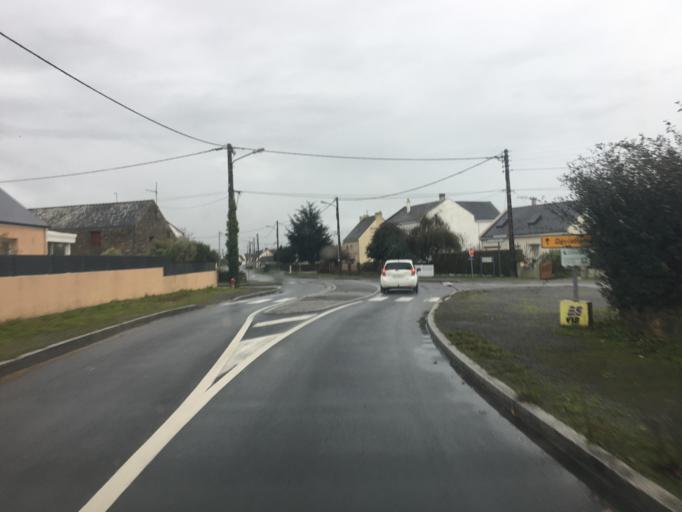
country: FR
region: Pays de la Loire
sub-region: Departement de la Loire-Atlantique
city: La Turballe
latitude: 47.3494
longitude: -2.4871
